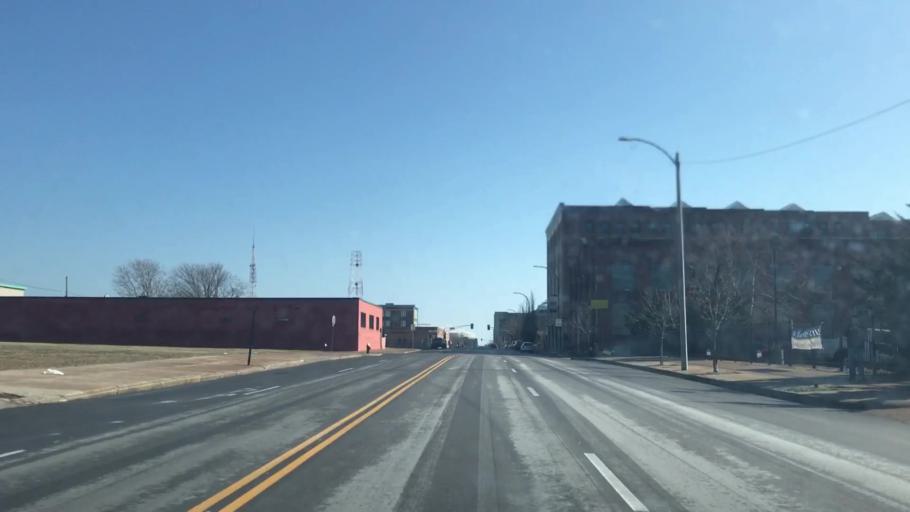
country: US
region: Missouri
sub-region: City of Saint Louis
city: St. Louis
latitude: 38.6361
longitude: -90.2095
